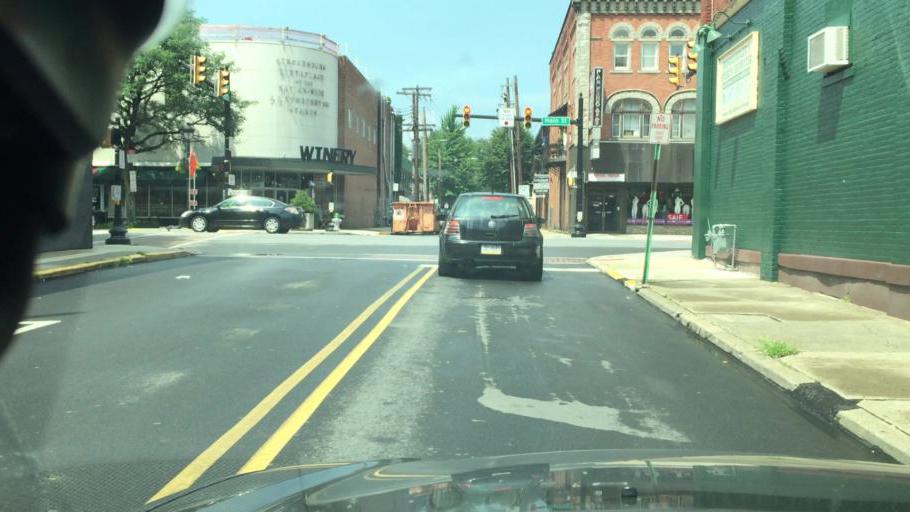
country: US
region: Pennsylvania
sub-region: Monroe County
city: Stroudsburg
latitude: 40.9854
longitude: -75.1930
